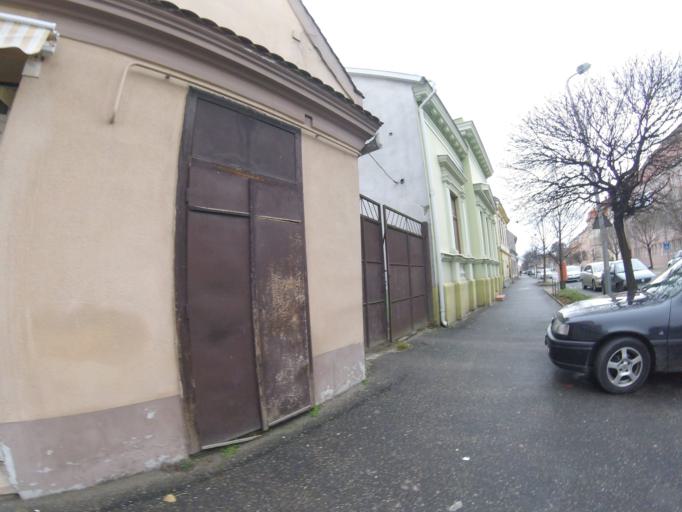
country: HU
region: Veszprem
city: Papa
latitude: 47.3269
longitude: 17.4712
